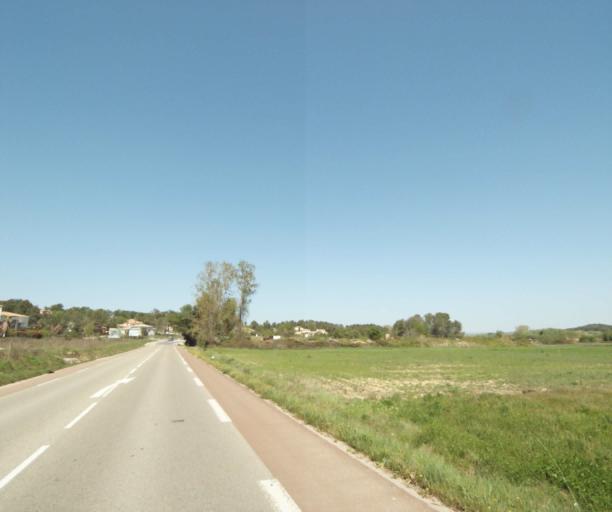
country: FR
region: Languedoc-Roussillon
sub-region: Departement de l'Herault
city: Montferrier-sur-Lez
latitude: 43.6759
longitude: 3.8573
